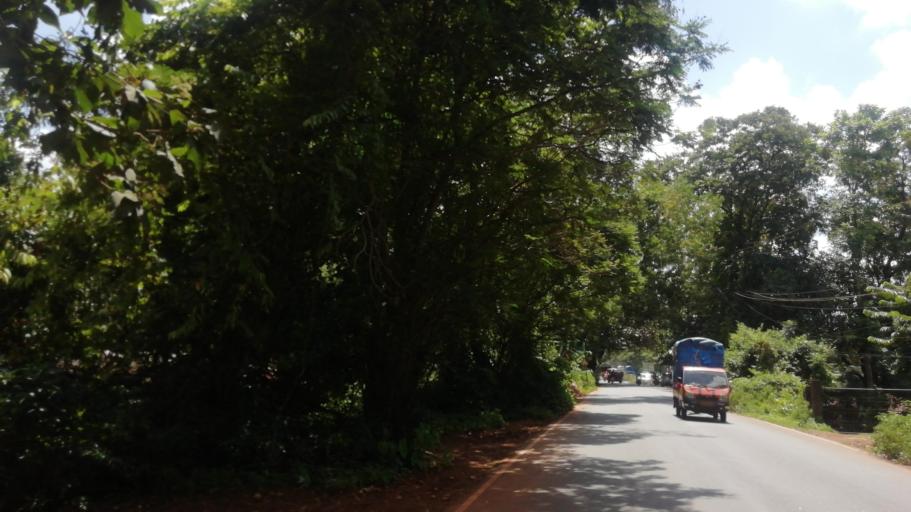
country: IN
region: Goa
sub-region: North Goa
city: Queula
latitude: 15.3845
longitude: 74.0043
